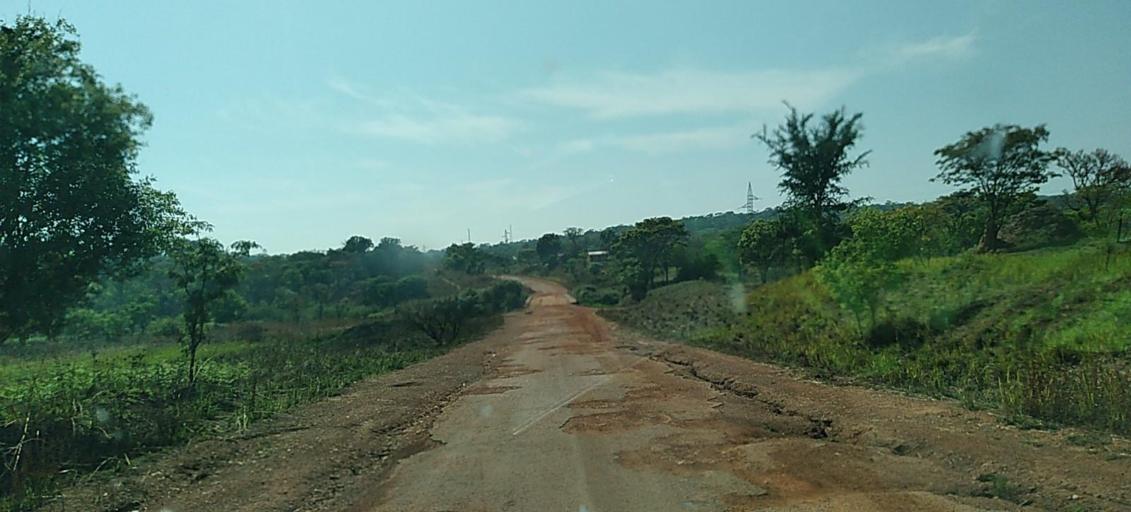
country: ZM
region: North-Western
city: Mwinilunga
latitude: -11.8250
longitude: 25.1242
